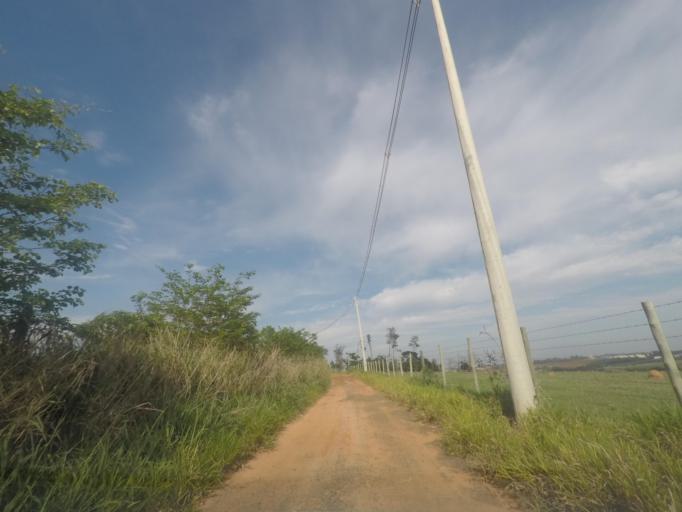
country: BR
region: Sao Paulo
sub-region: Sumare
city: Sumare
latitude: -22.7853
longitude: -47.2376
